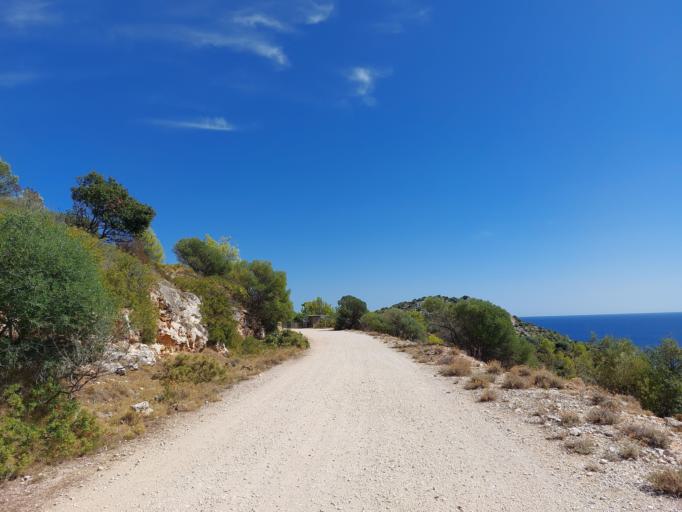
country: HR
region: Dubrovacko-Neretvanska
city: Smokvica
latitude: 42.7336
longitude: 16.8369
